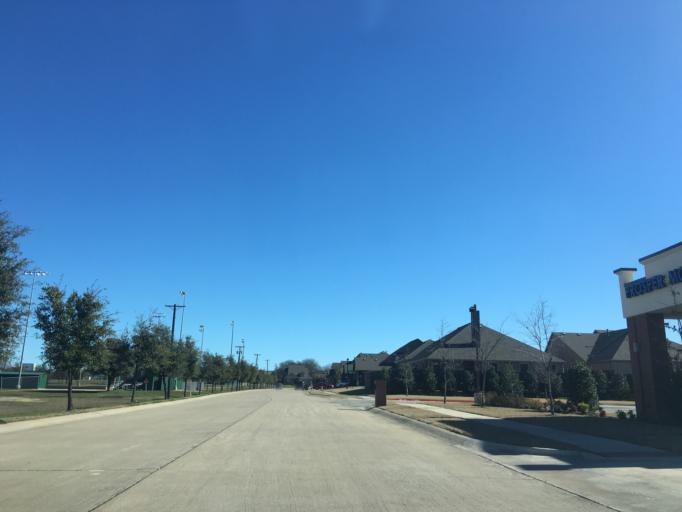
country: US
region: Texas
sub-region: Collin County
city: Prosper
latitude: 33.2408
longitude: -96.8019
